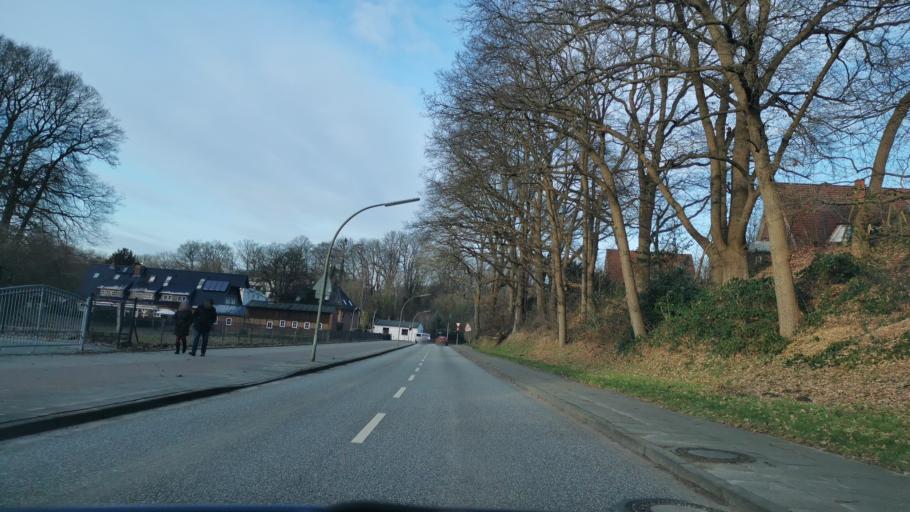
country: DE
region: Hamburg
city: Harburg
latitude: 53.4346
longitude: 9.9689
